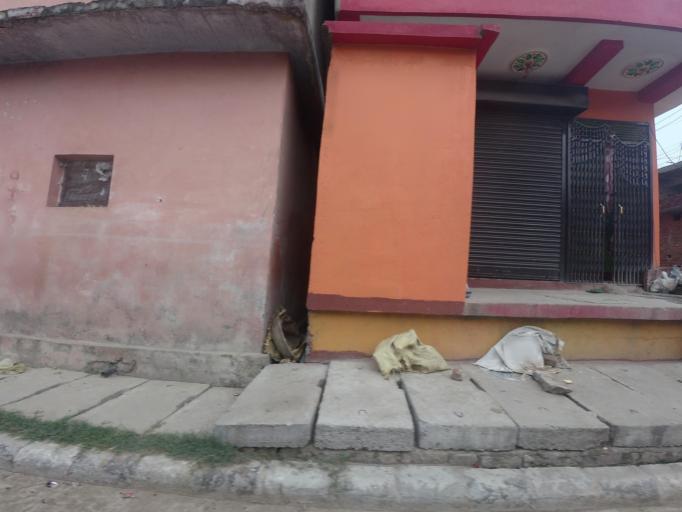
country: NP
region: Western Region
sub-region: Lumbini Zone
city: Bhairahawa
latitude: 27.5107
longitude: 83.4247
